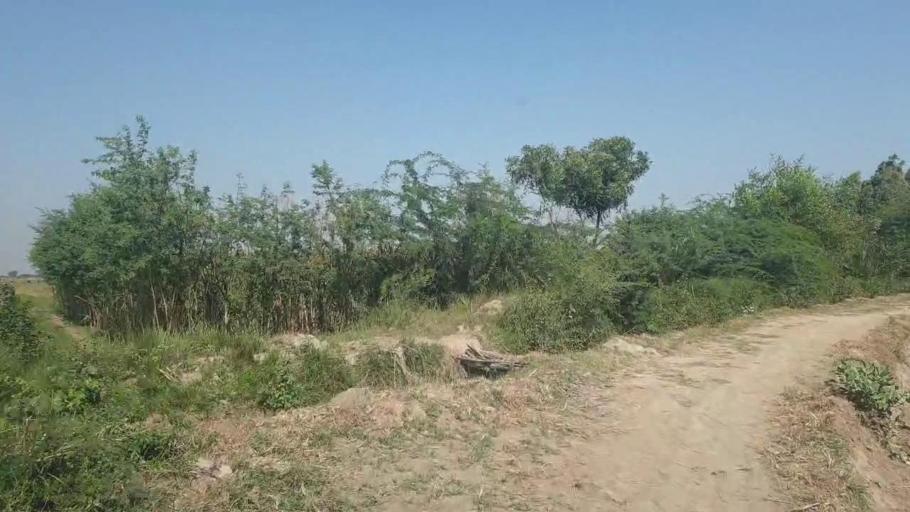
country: PK
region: Sindh
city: Badin
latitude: 24.6817
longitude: 68.8933
